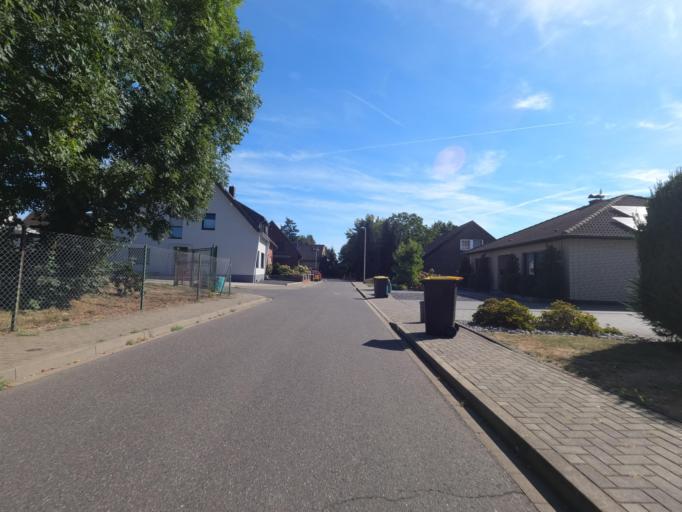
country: DE
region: North Rhine-Westphalia
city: Erkelenz
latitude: 51.0336
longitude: 6.3597
